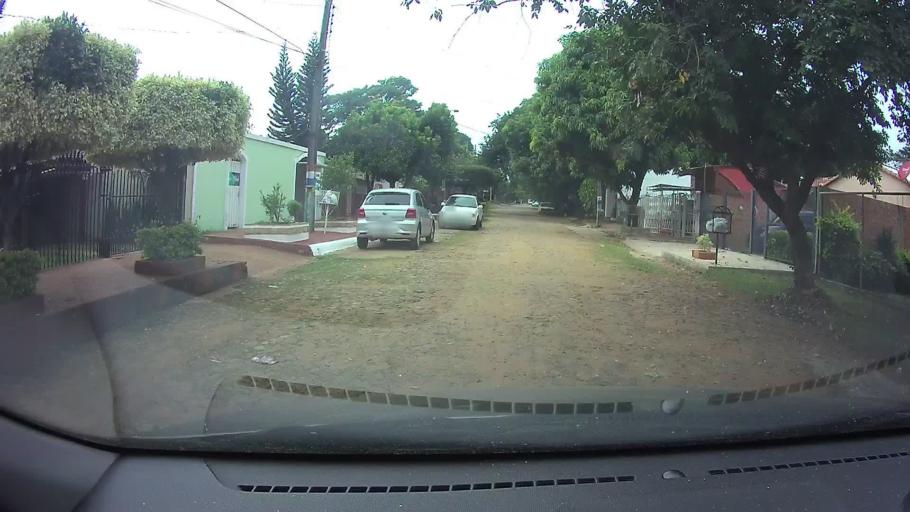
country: PY
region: Central
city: Limpio
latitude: -25.2371
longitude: -57.4801
